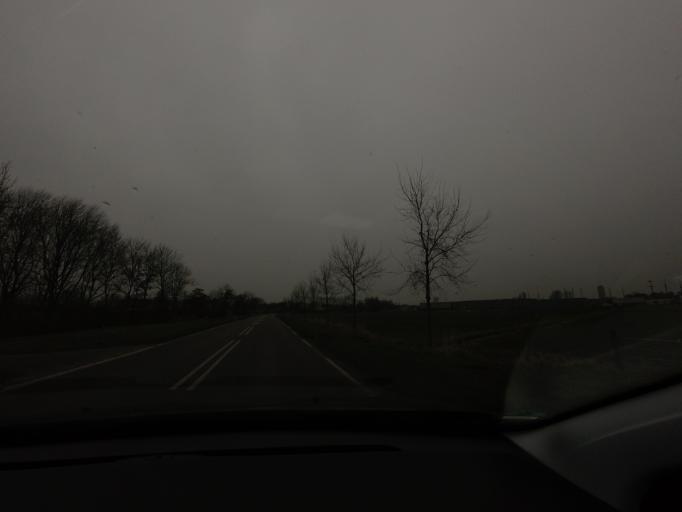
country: NL
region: Friesland
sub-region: Gemeente Franekeradeel
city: Franeker
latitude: 53.1794
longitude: 5.5577
